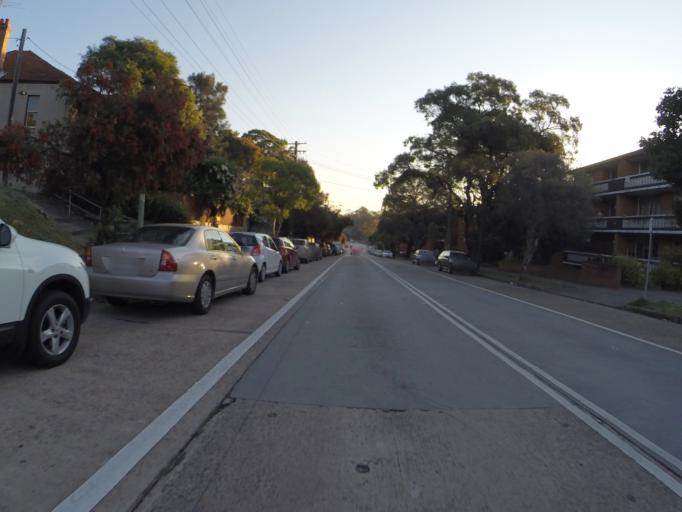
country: AU
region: New South Wales
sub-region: Marrickville
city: Marrickville
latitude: -33.9177
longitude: 151.1479
